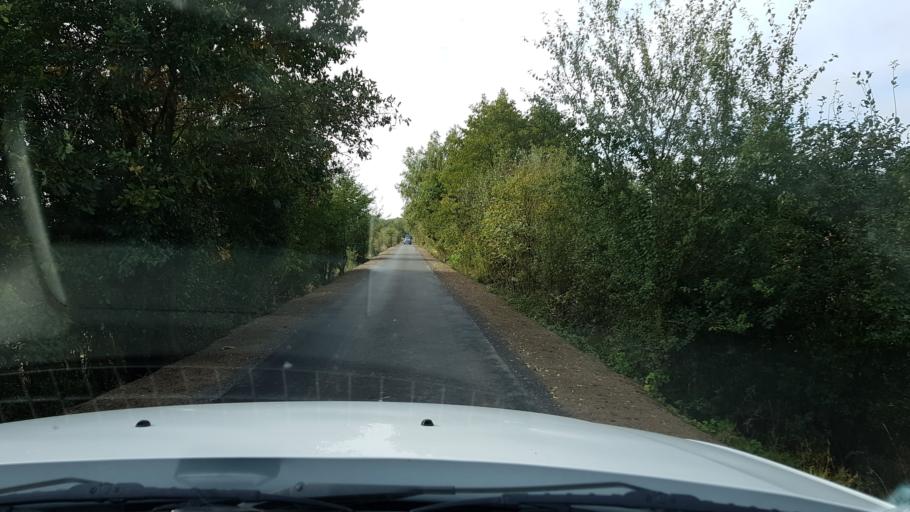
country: PL
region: West Pomeranian Voivodeship
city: Trzcinsko Zdroj
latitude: 52.9465
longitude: 14.5743
